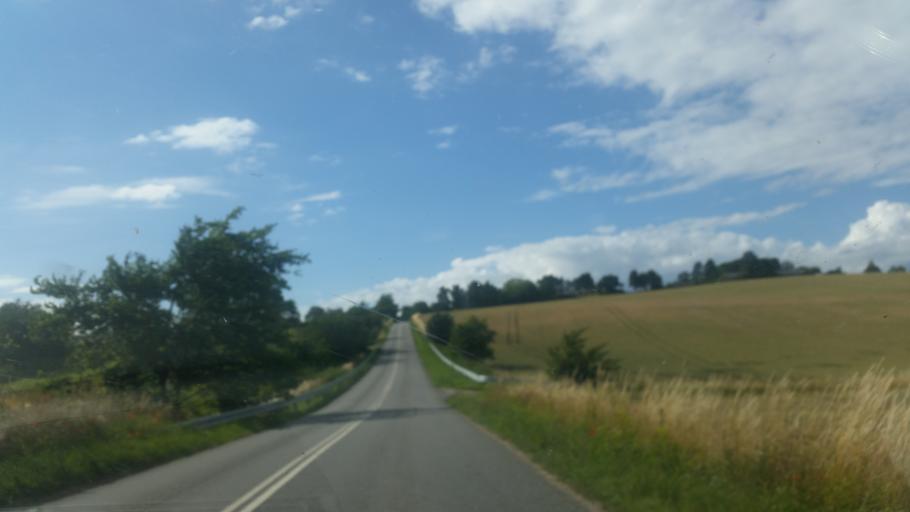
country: DK
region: Zealand
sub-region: Odsherred Kommune
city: Horve
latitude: 55.8140
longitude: 11.4258
